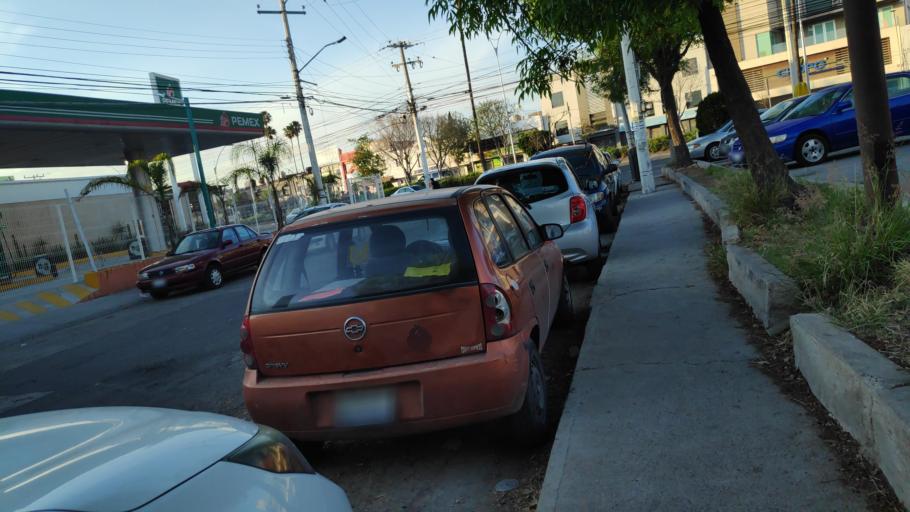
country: MX
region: Queretaro
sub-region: Queretaro
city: Santiago de Queretaro
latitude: 20.5863
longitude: -100.3834
